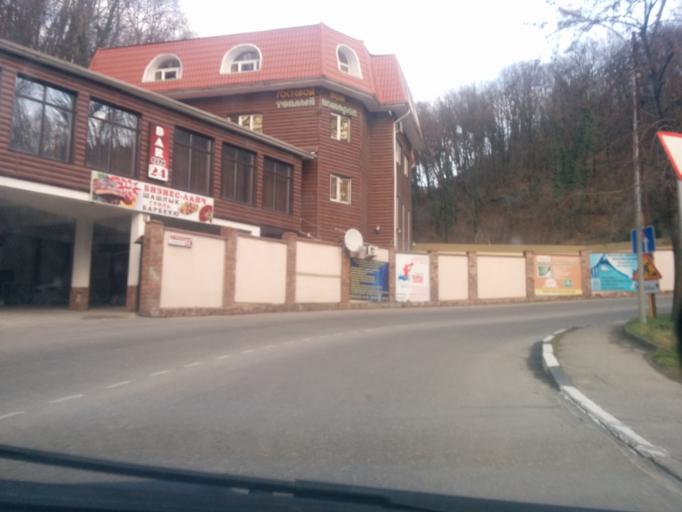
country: RU
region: Krasnodarskiy
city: Tuapse
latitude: 44.1077
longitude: 39.0633
